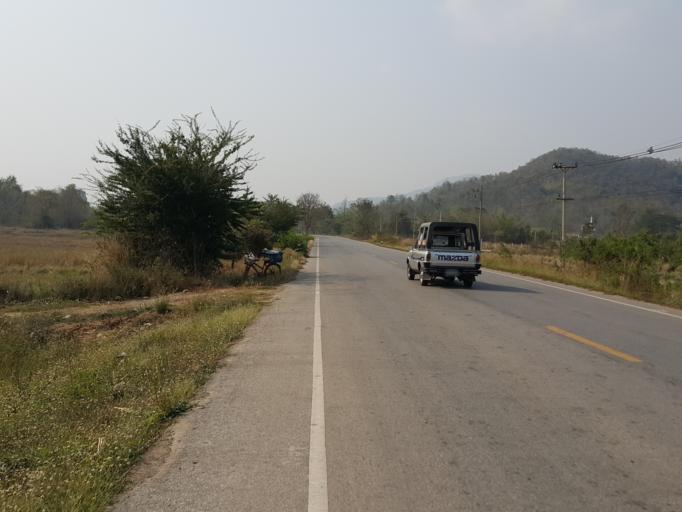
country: TH
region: Sukhothai
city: Thung Saliam
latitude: 17.3331
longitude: 99.4961
